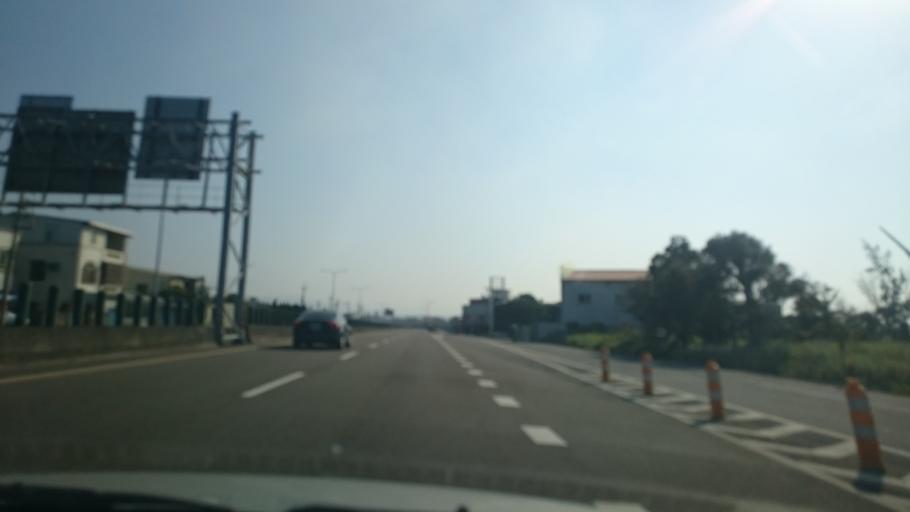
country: TW
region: Taiwan
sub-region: Hsinchu
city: Hsinchu
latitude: 24.7167
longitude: 120.8676
